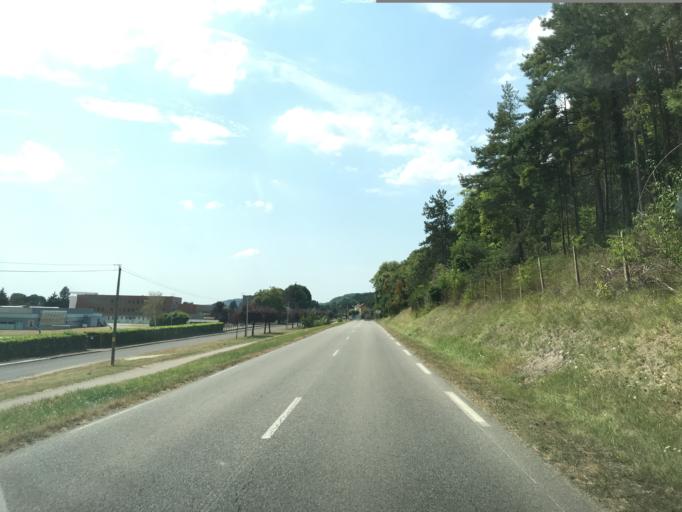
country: FR
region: Centre
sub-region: Departement d'Eure-et-Loir
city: Anet
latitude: 48.8700
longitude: 1.4337
